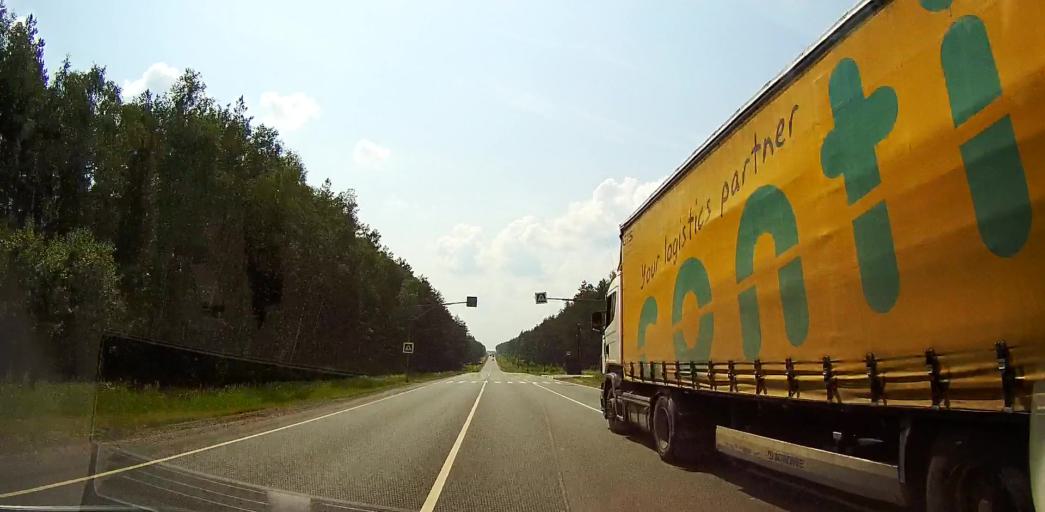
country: RU
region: Moskovskaya
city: Meshcherino
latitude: 55.1725
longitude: 38.3309
